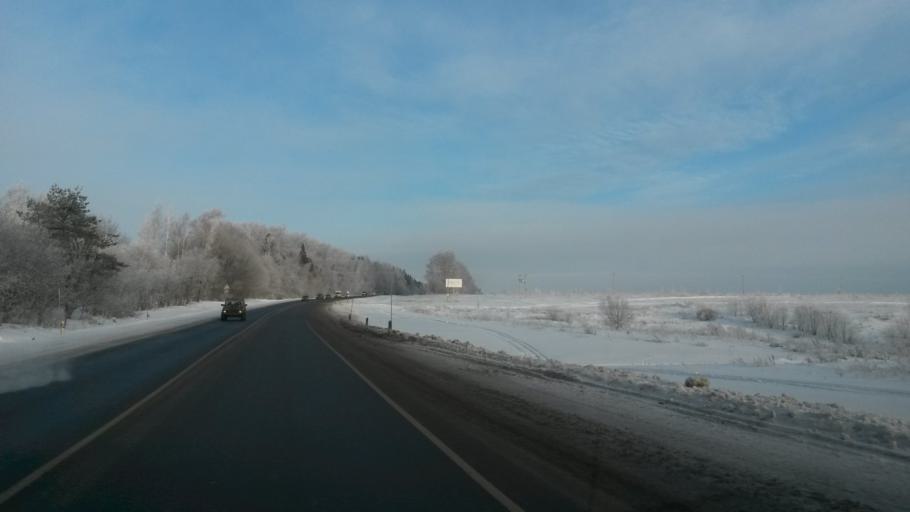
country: RU
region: Vladimir
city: Bogolyubovo
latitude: 56.2234
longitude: 40.4422
